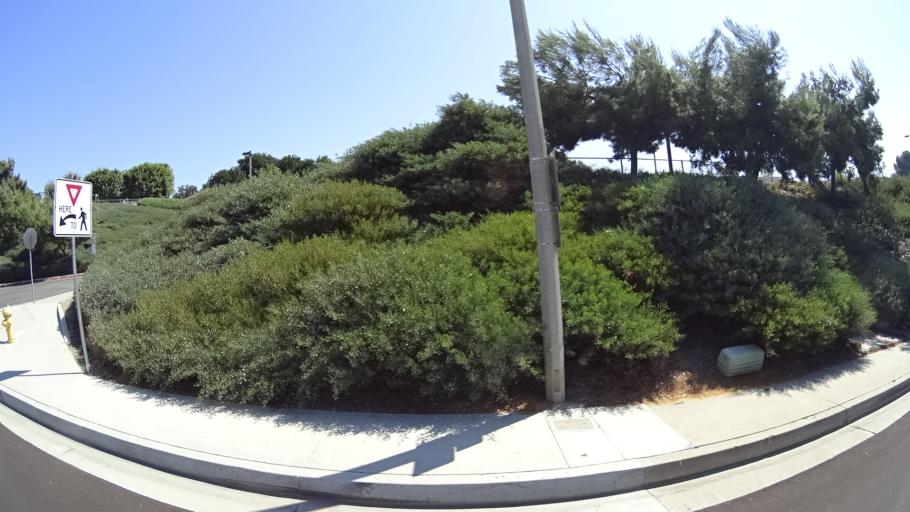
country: US
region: California
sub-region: Orange County
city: San Clemente
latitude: 33.4679
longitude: -117.6261
